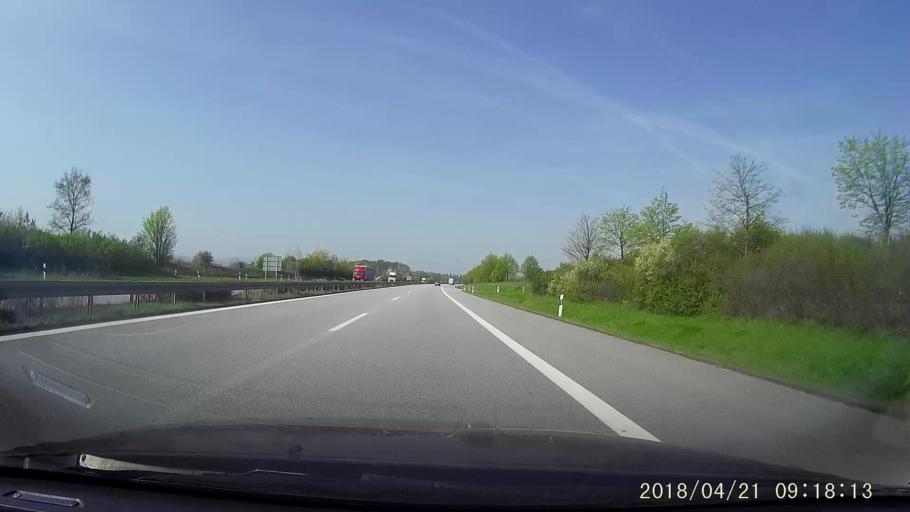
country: DE
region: Saxony
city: Weissenberg
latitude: 51.2073
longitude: 14.6840
